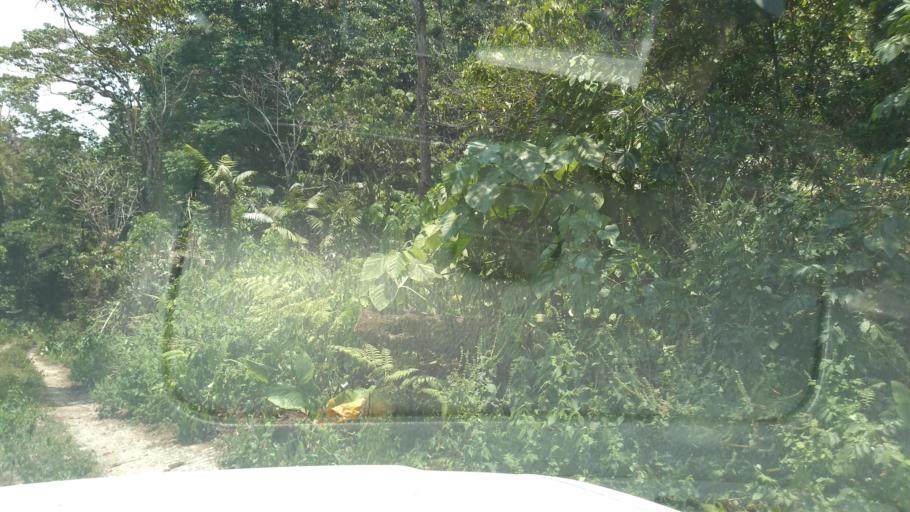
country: MX
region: Veracruz
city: Motzorongo
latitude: 18.6073
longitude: -96.7597
